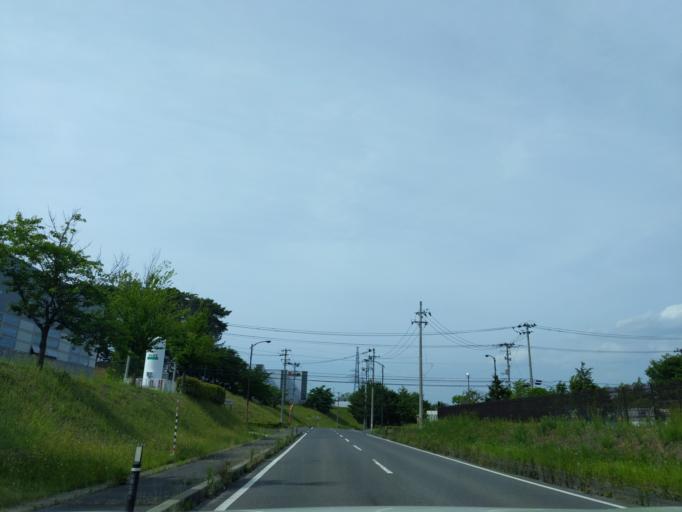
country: JP
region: Fukushima
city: Koriyama
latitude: 37.4491
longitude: 140.3096
